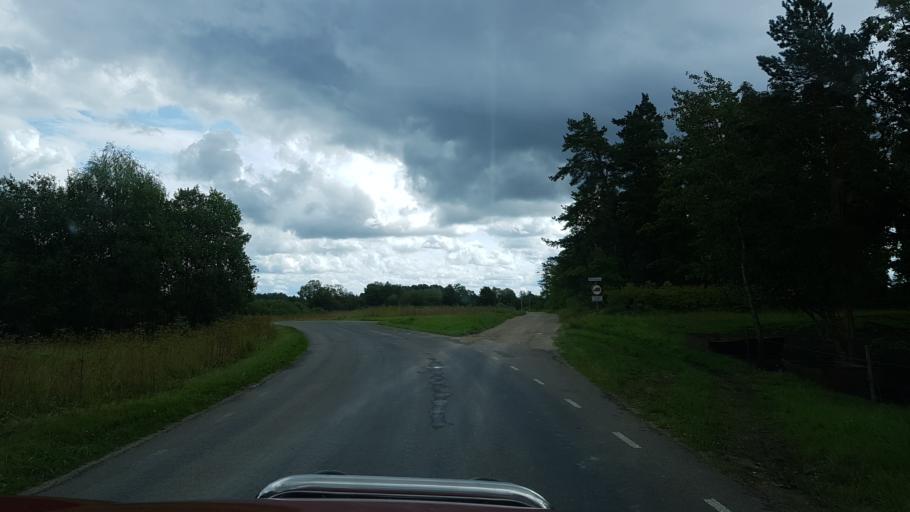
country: EE
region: Laeaene
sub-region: Lihula vald
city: Lihula
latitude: 58.7221
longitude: 23.9589
